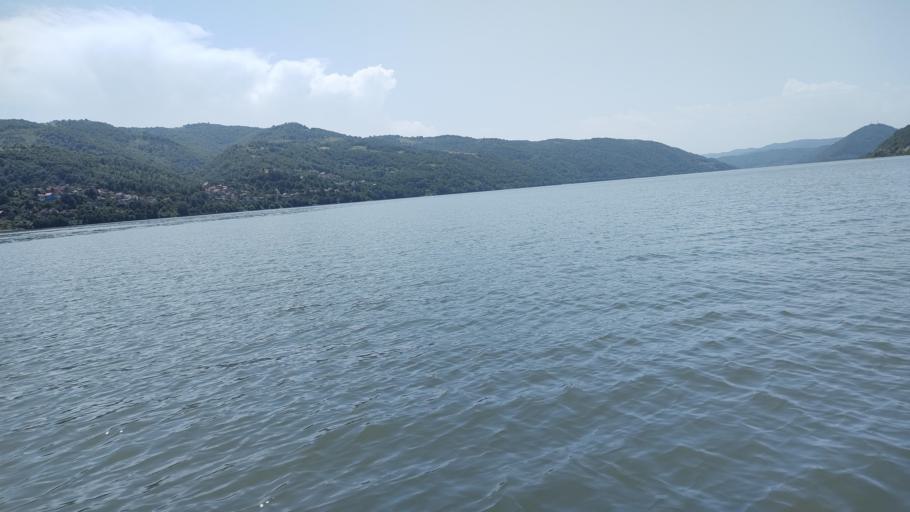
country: RO
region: Mehedinti
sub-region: Comuna Svinita
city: Svinita
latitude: 44.5095
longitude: 22.1951
